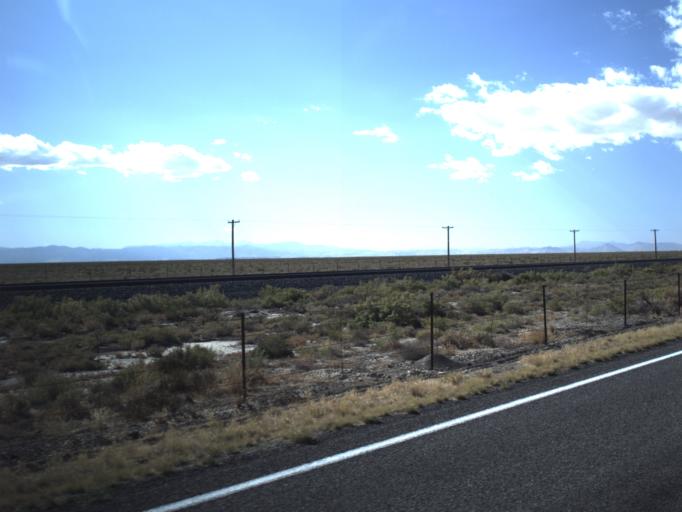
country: US
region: Utah
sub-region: Millard County
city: Delta
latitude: 39.1370
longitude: -112.7274
